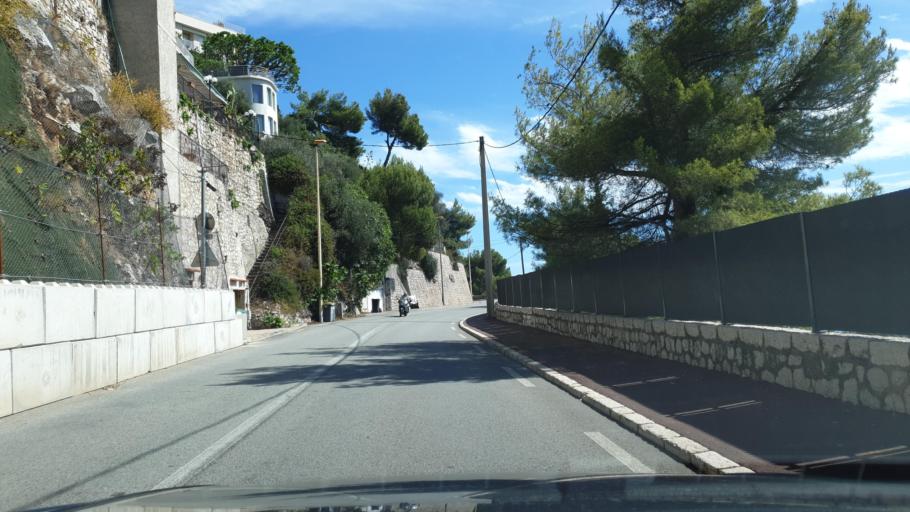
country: FR
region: Provence-Alpes-Cote d'Azur
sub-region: Departement des Alpes-Maritimes
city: Villefranche-sur-Mer
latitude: 43.7103
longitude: 7.3144
